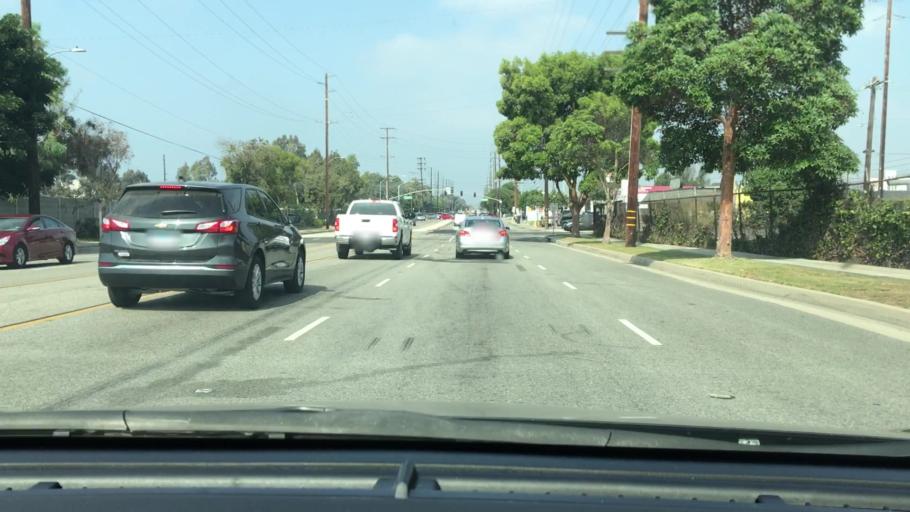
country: US
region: California
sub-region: Los Angeles County
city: Torrance
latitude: 33.8584
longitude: -118.3257
